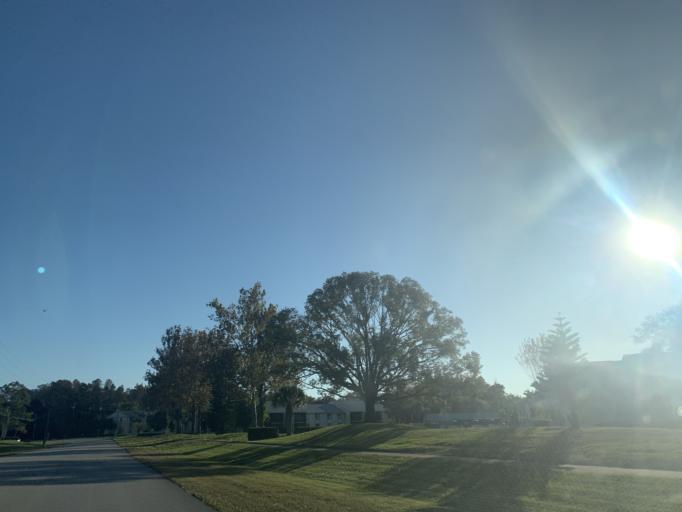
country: US
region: Florida
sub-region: Pinellas County
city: East Lake
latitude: 28.1232
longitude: -82.6913
